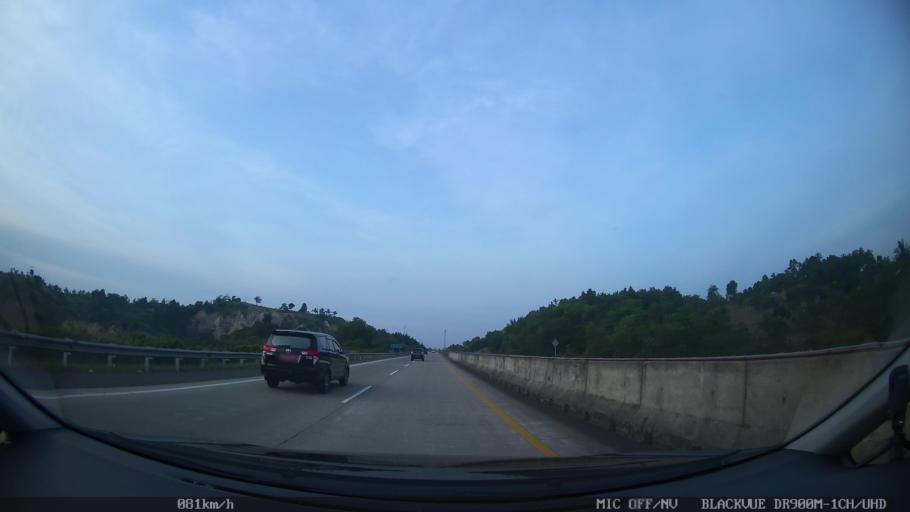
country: ID
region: Lampung
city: Penengahan
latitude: -5.8303
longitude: 105.7326
